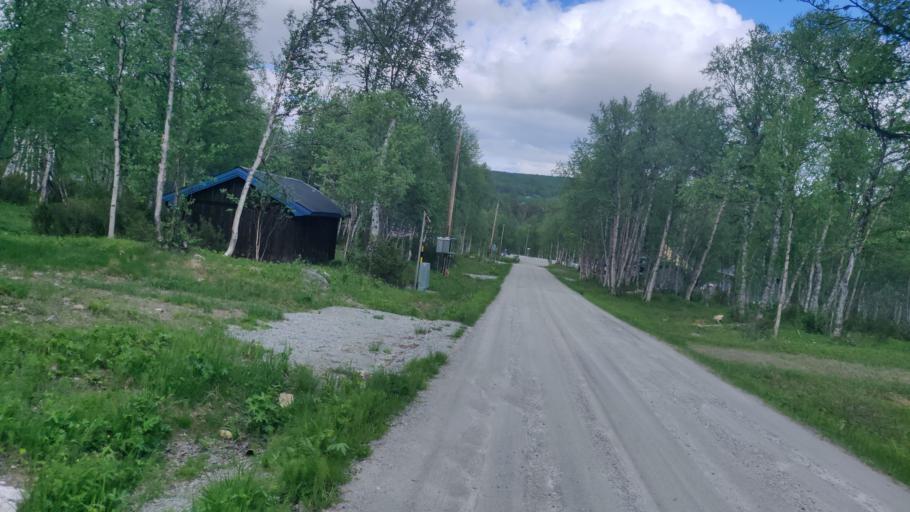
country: NO
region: Sor-Trondelag
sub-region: Tydal
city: Aas
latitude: 62.6427
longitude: 12.4130
